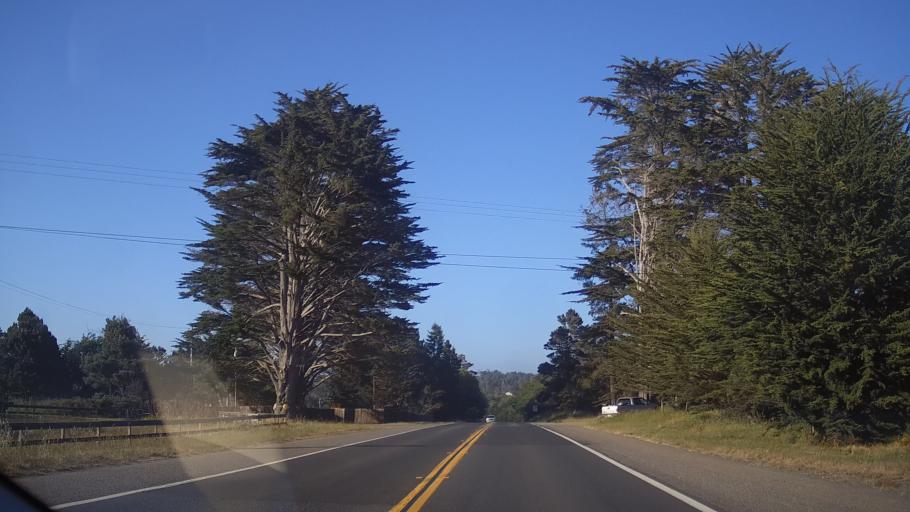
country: US
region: California
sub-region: Mendocino County
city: Fort Bragg
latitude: 39.4842
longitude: -123.7913
